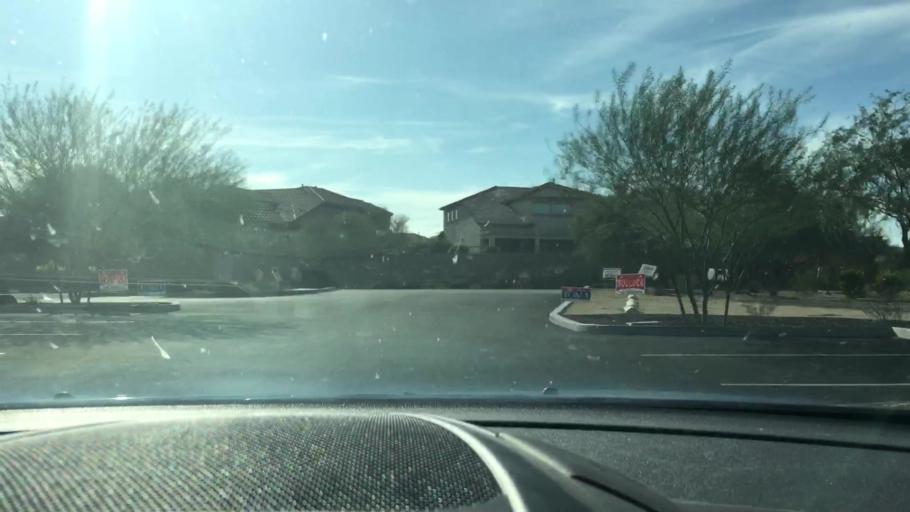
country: US
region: Arizona
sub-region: Maricopa County
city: Sun City West
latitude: 33.7292
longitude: -112.2518
